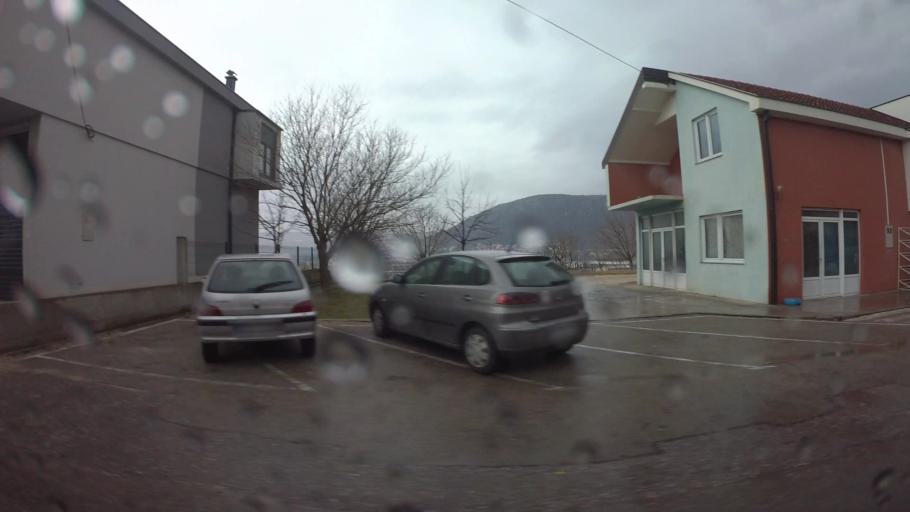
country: BA
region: Federation of Bosnia and Herzegovina
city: Rodoc
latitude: 43.3164
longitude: 17.8365
